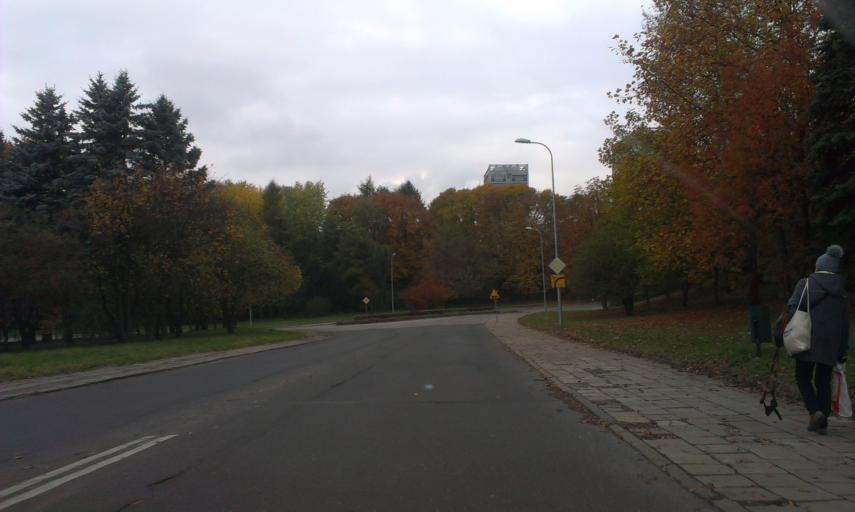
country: PL
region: West Pomeranian Voivodeship
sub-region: Koszalin
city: Koszalin
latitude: 54.1980
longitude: 16.1799
